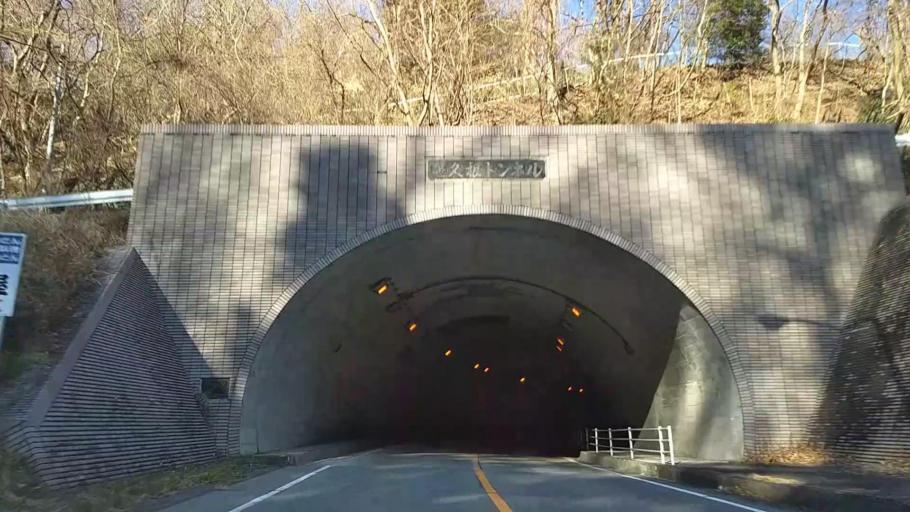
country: JP
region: Yamanashi
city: Uenohara
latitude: 35.5362
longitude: 139.0785
